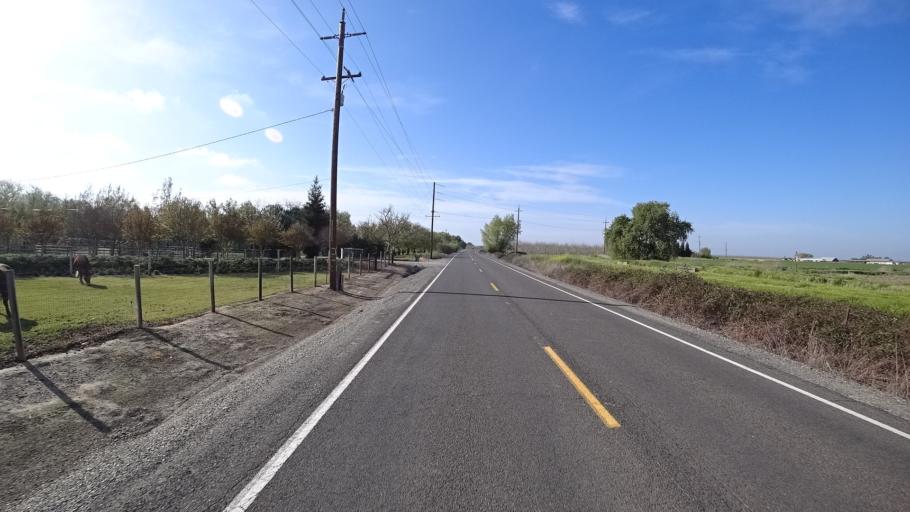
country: US
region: California
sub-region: Glenn County
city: Hamilton City
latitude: 39.5874
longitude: -122.0075
